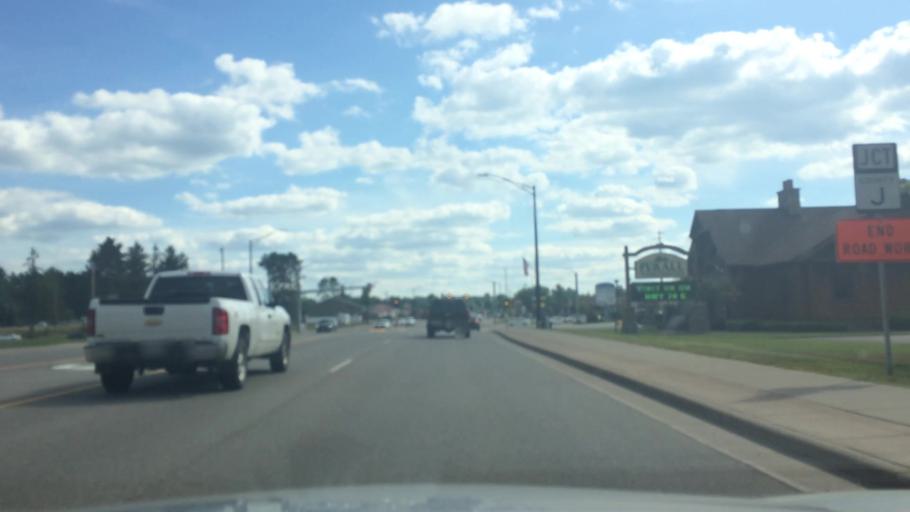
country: US
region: Wisconsin
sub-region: Vilas County
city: Lac du Flambeau
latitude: 45.8920
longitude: -89.7004
